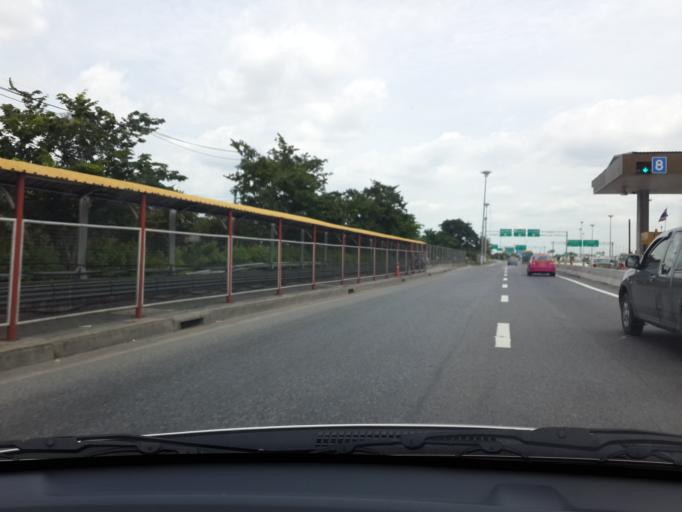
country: TH
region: Bangkok
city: Saphan Sung
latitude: 13.7744
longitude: 100.6886
